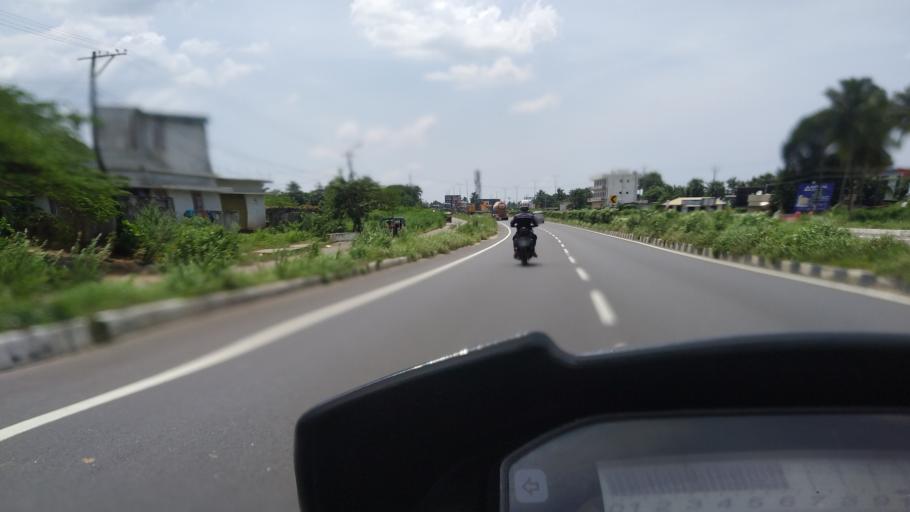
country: IN
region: Kerala
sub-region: Palakkad district
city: Chittur
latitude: 10.8008
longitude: 76.7831
